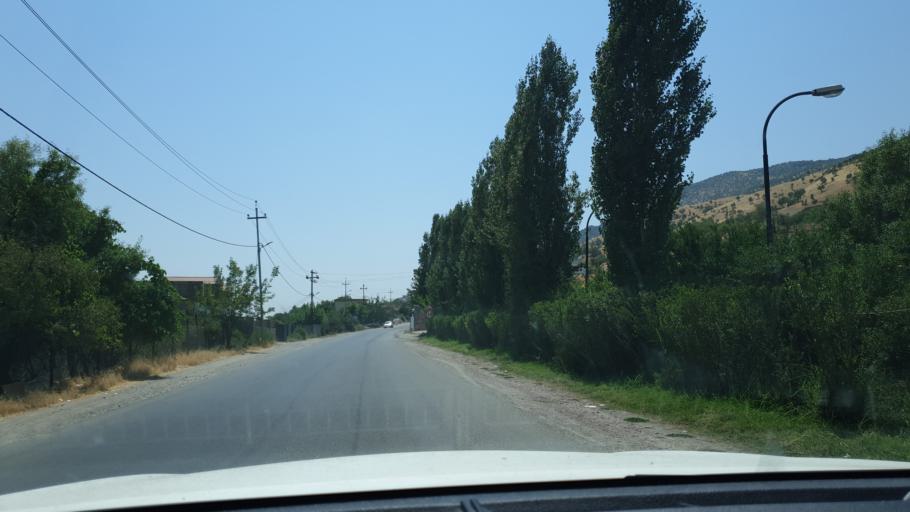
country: IQ
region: Arbil
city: Nahiyat Hiran
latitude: 36.2967
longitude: 44.4733
